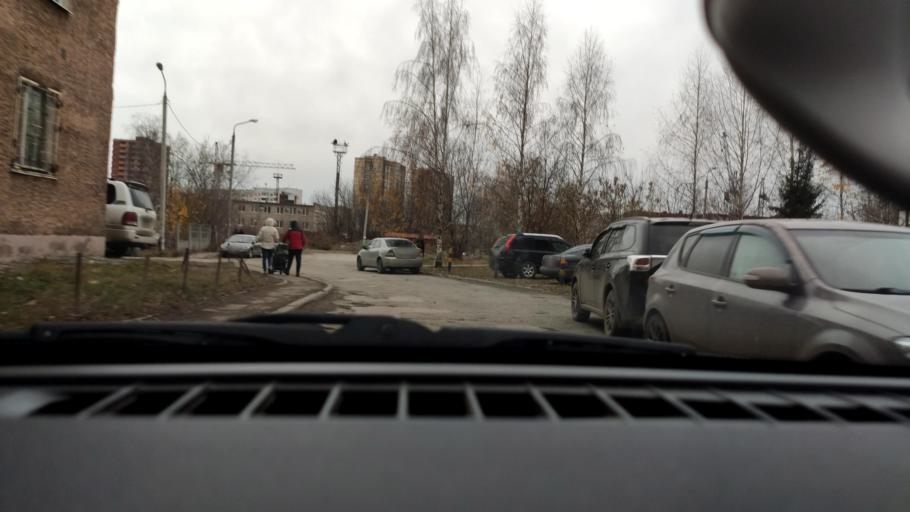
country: RU
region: Perm
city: Perm
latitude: 57.9696
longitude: 56.1939
